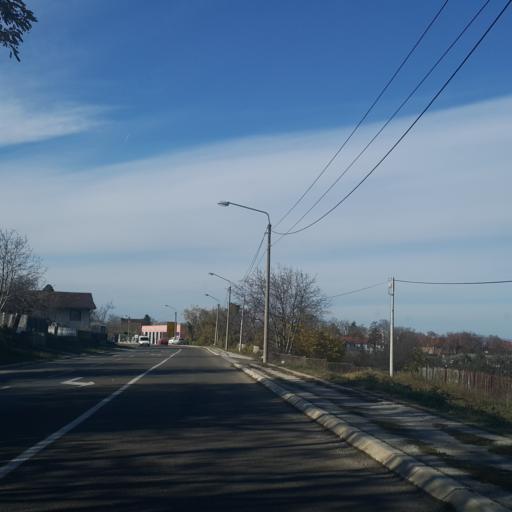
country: RS
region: Central Serbia
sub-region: Sumadijski Okrug
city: Topola
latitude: 44.2551
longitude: 20.6857
